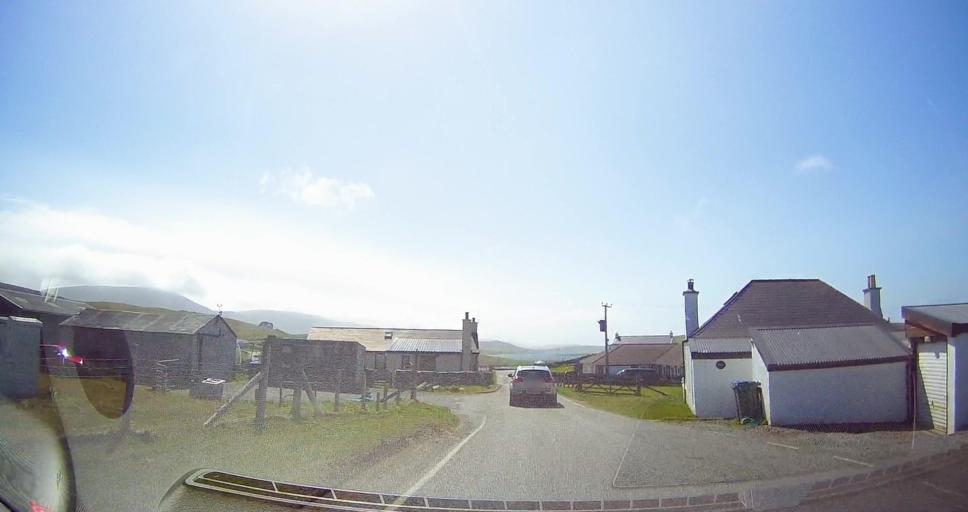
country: GB
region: Scotland
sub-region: Shetland Islands
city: Sandwick
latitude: 60.0846
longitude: -1.3321
